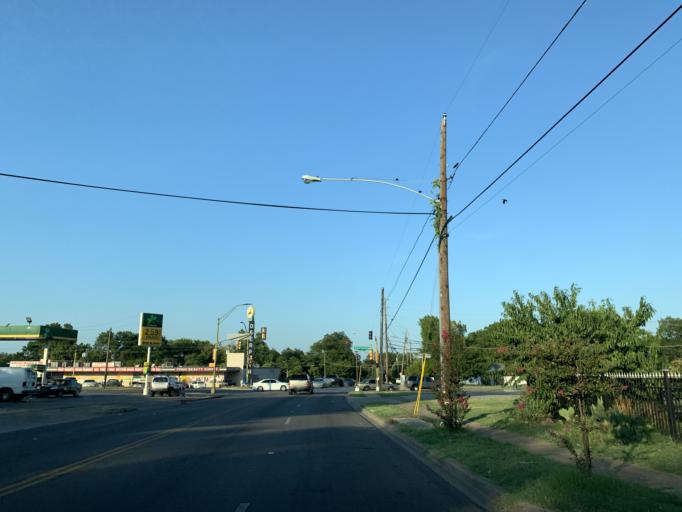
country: US
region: Texas
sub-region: Dallas County
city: Dallas
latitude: 32.7114
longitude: -96.7848
